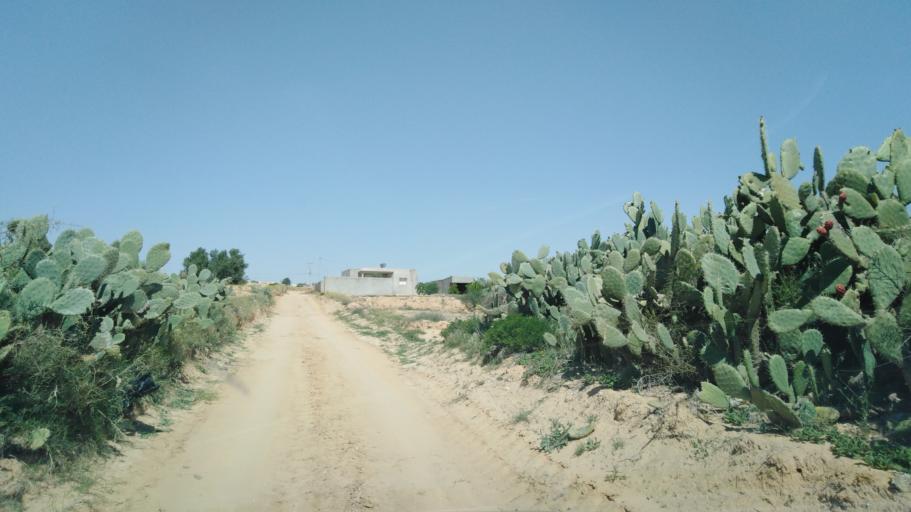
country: TN
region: Safaqis
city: Sfax
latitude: 34.7767
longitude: 10.5264
